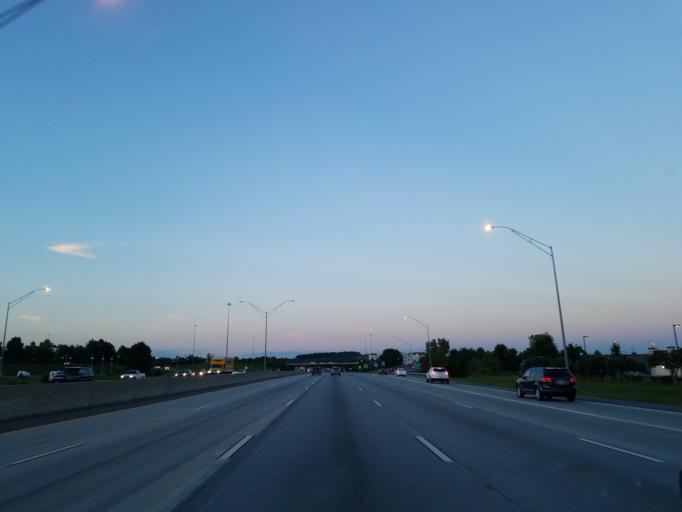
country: US
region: North Carolina
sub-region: Cabarrus County
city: Harrisburg
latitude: 35.3650
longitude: -80.7172
